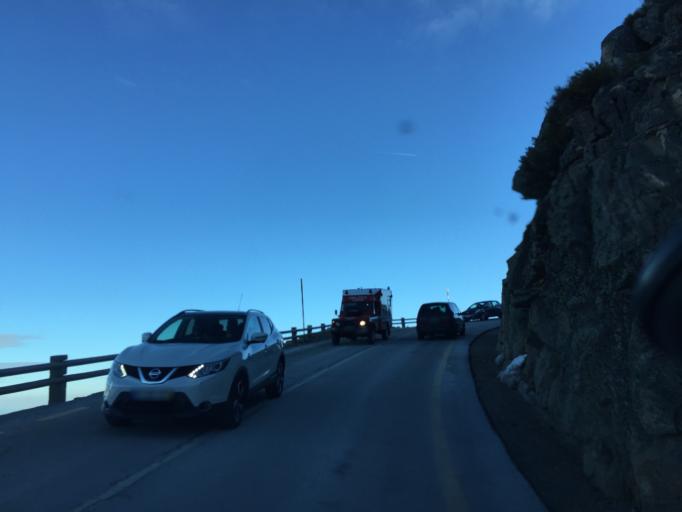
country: PT
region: Castelo Branco
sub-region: Covilha
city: Covilha
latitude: 40.3199
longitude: -7.5907
